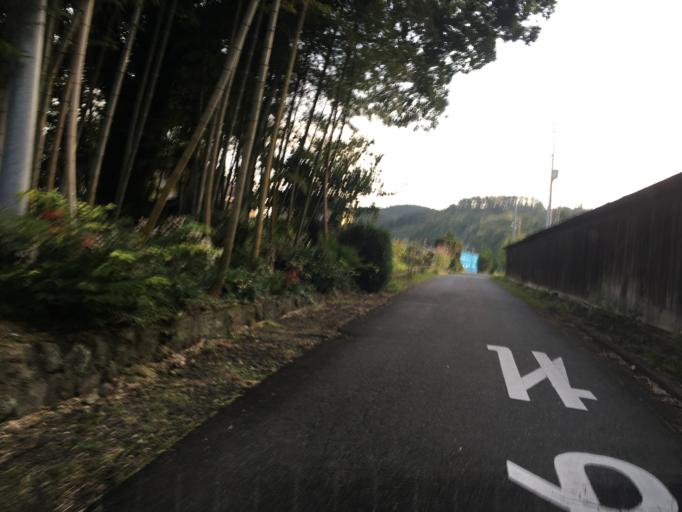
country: JP
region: Fukushima
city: Hobaramachi
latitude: 37.8747
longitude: 140.5194
